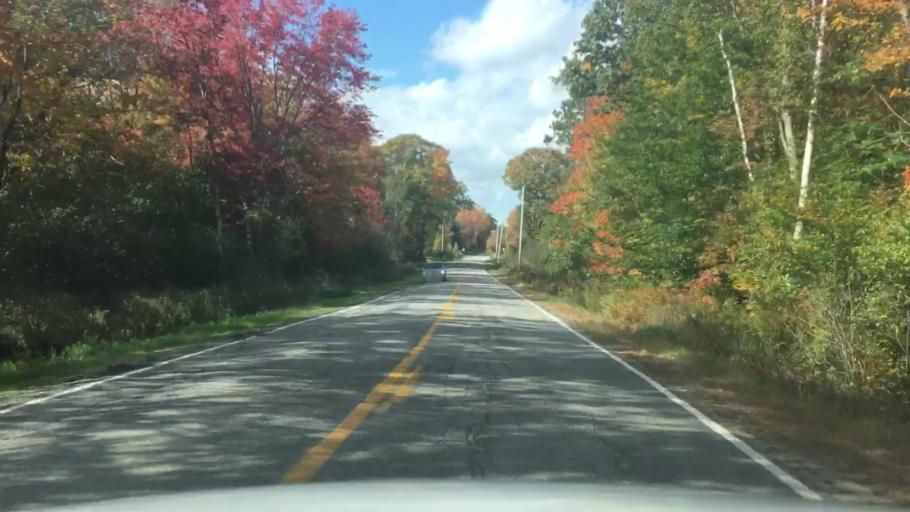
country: US
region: Maine
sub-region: Knox County
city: Appleton
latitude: 44.2732
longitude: -69.2841
